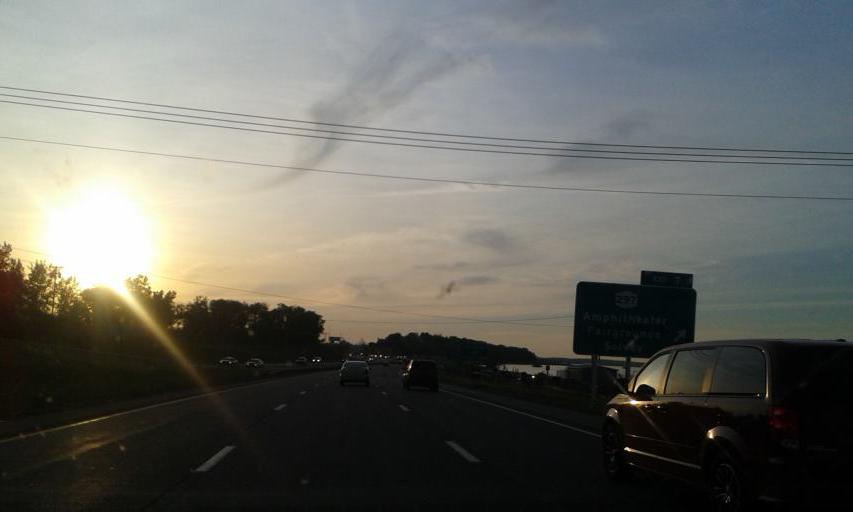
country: US
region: New York
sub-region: Onondaga County
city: Solvay
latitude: 43.0659
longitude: -76.1970
